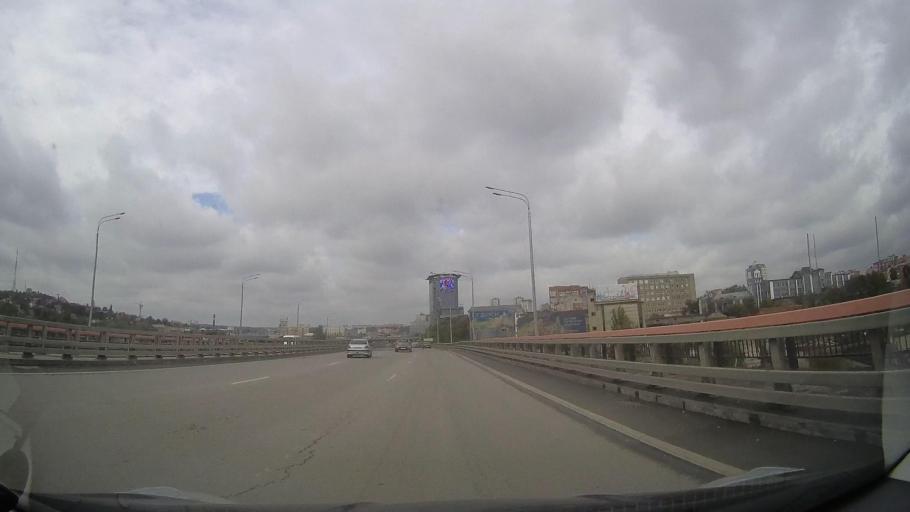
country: RU
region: Rostov
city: Rostov-na-Donu
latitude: 47.2116
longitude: 39.7016
